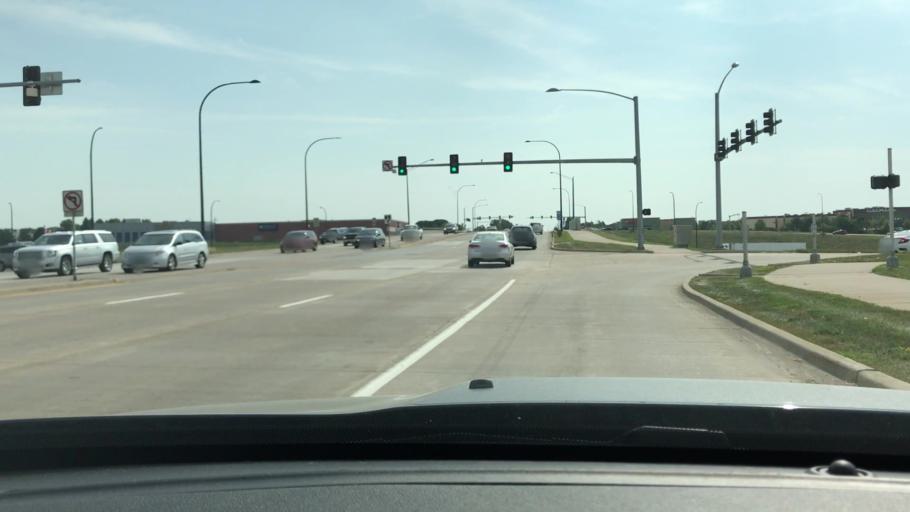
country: US
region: Iowa
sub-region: Scott County
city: Bettendorf
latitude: 41.5747
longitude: -90.5243
